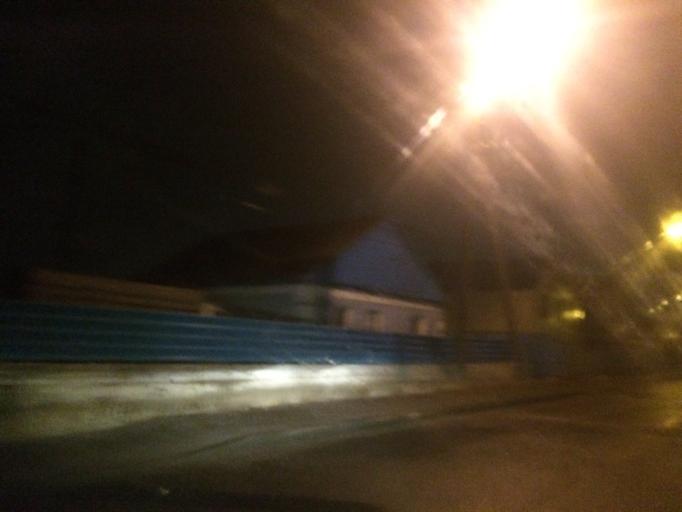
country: KZ
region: Astana Qalasy
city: Astana
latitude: 51.1964
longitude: 71.3827
